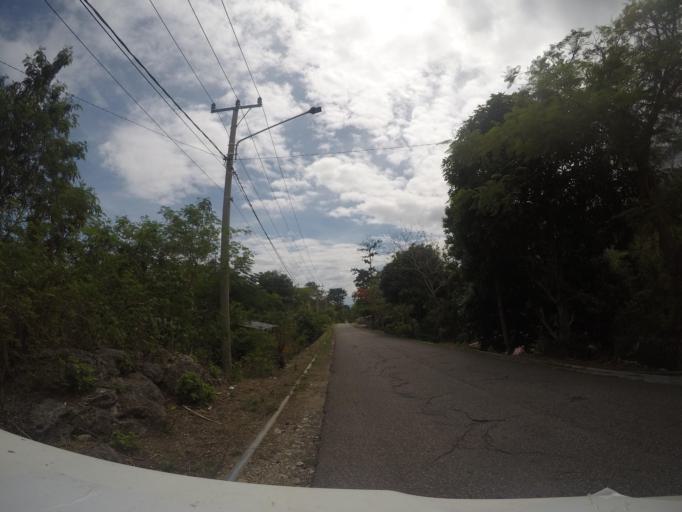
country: TL
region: Baucau
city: Baucau
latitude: -8.4620
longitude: 126.4406
